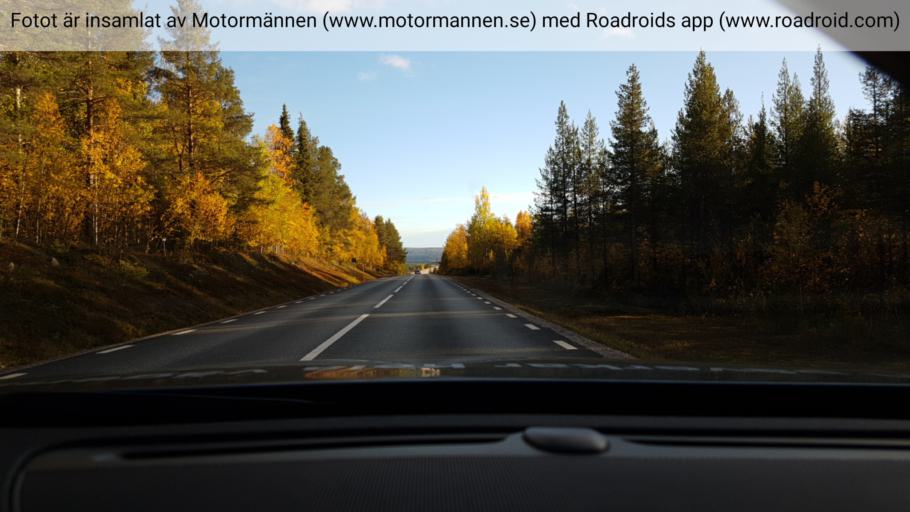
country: SE
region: Norrbotten
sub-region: Jokkmokks Kommun
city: Jokkmokk
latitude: 66.8961
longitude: 19.8273
